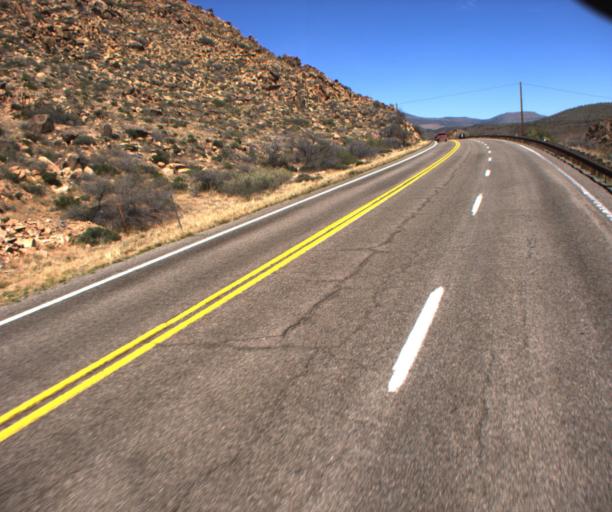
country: US
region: Arizona
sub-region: Mohave County
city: Peach Springs
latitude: 35.4134
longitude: -113.6469
